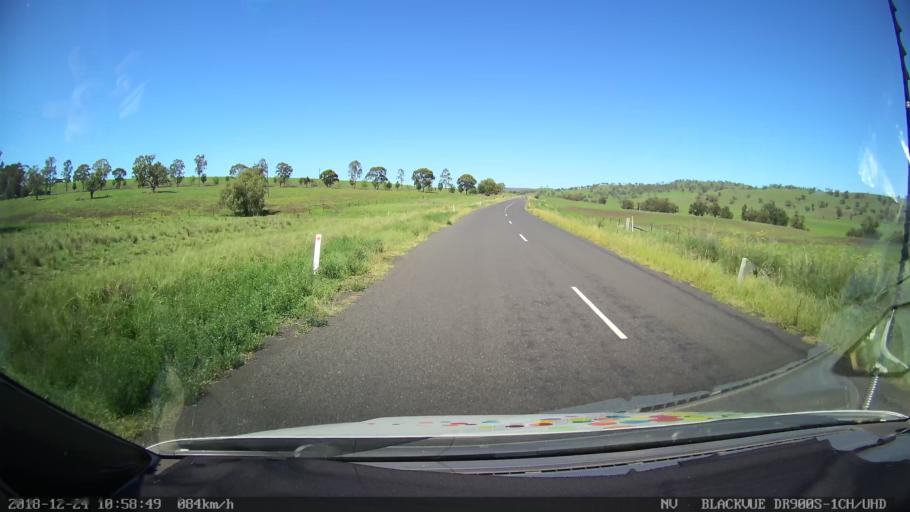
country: AU
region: New South Wales
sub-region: Upper Hunter Shire
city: Merriwa
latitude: -32.0517
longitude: 150.4044
